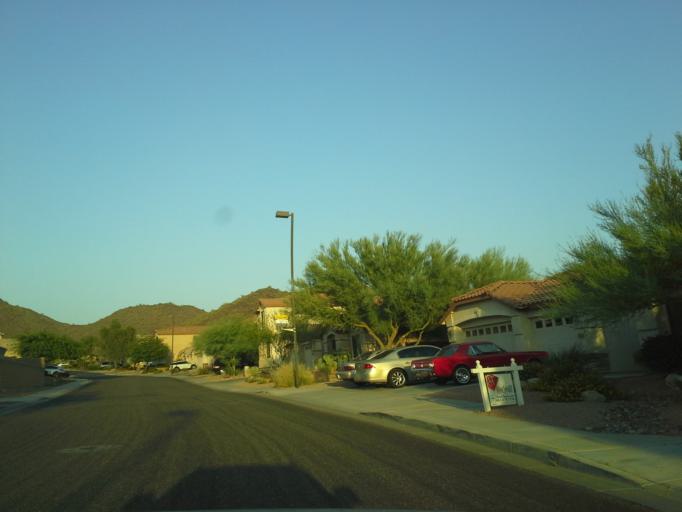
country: US
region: Arizona
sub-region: Maricopa County
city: Anthem
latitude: 33.7522
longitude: -112.1047
